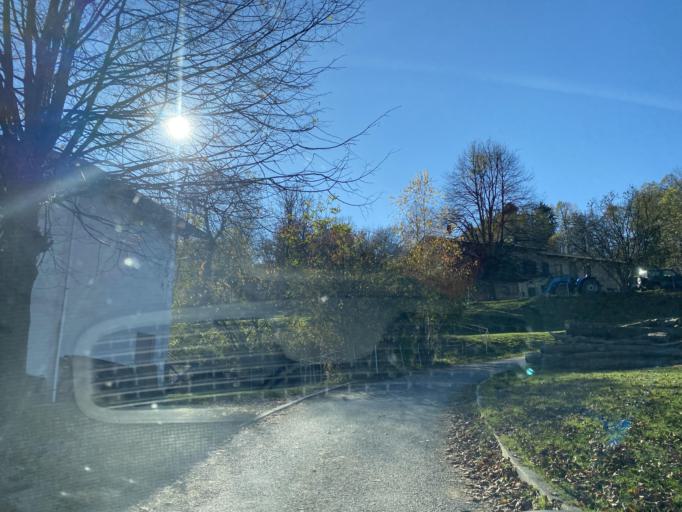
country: IT
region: Lombardy
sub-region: Provincia di Como
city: Pellio Intelvi
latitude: 45.9747
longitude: 9.0578
